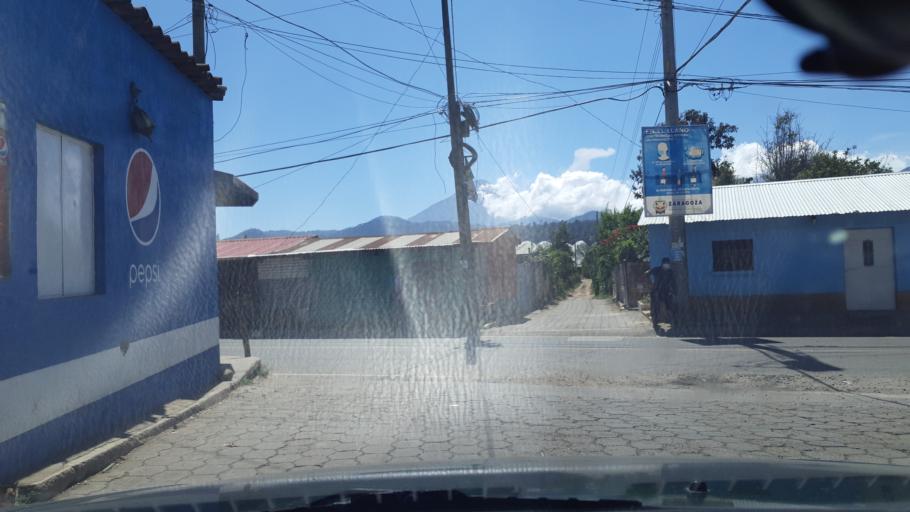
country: GT
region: Chimaltenango
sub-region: Municipio de Zaragoza
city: Zaragoza
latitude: 14.6590
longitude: -90.8630
